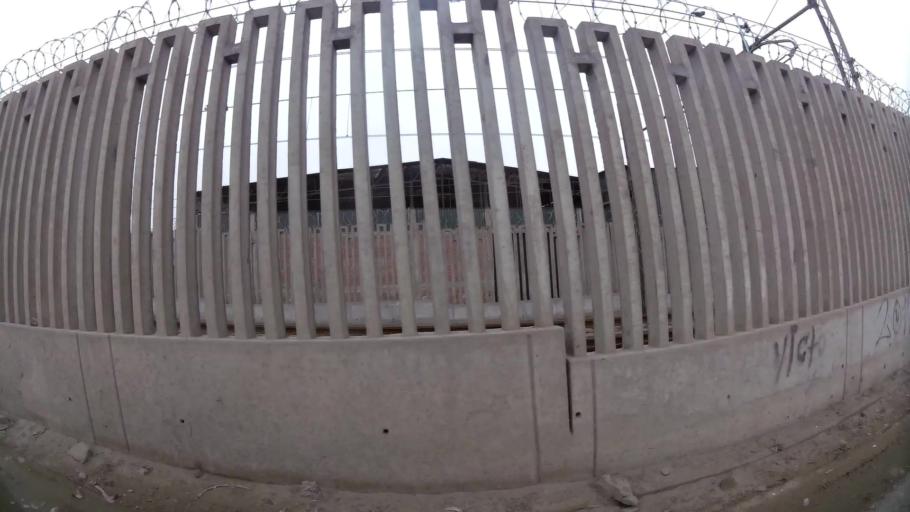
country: PE
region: Lima
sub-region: Lima
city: Surco
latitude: -12.1757
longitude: -76.9493
